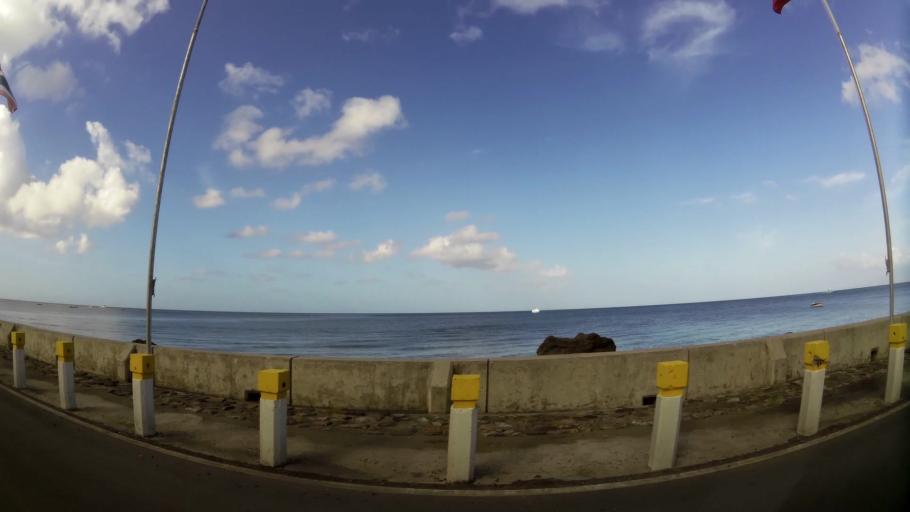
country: KN
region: Saint Paul Charlestown
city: Charlestown
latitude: 17.1417
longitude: -62.6299
